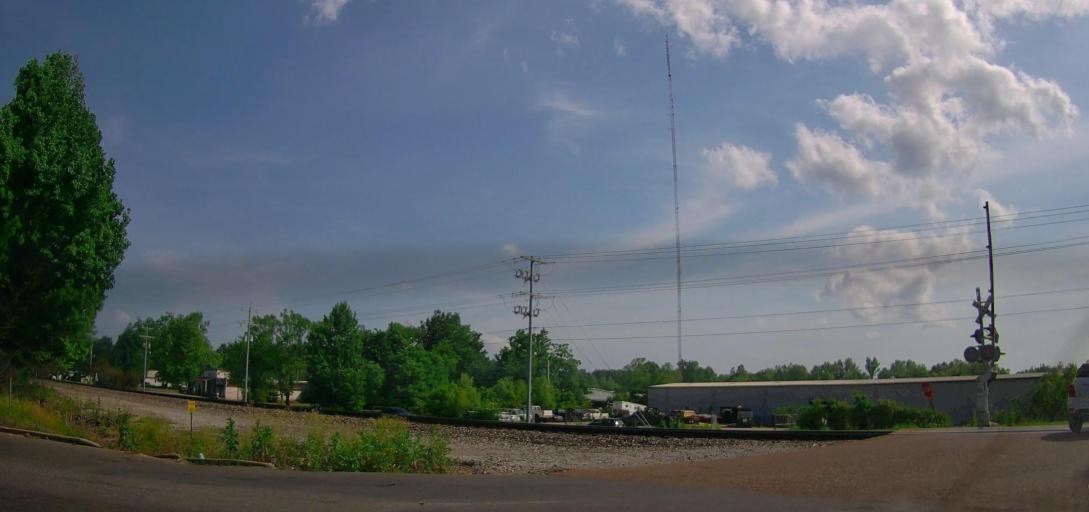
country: US
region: Mississippi
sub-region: De Soto County
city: Olive Branch
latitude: 34.9914
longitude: -89.8617
